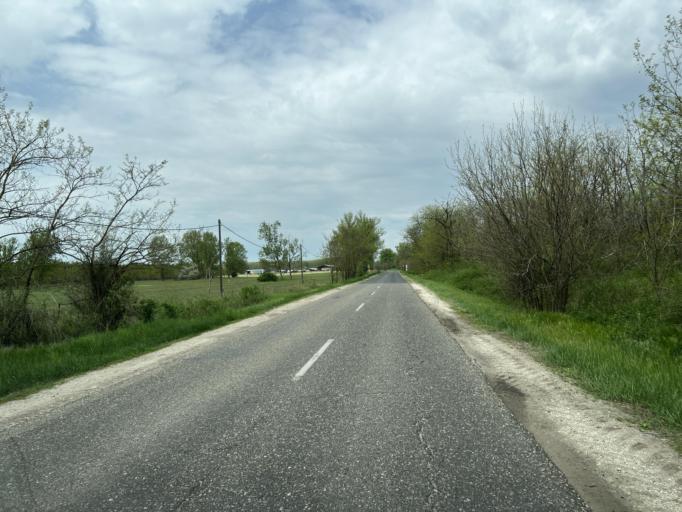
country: HU
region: Pest
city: Tortel
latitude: 47.1378
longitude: 19.8915
